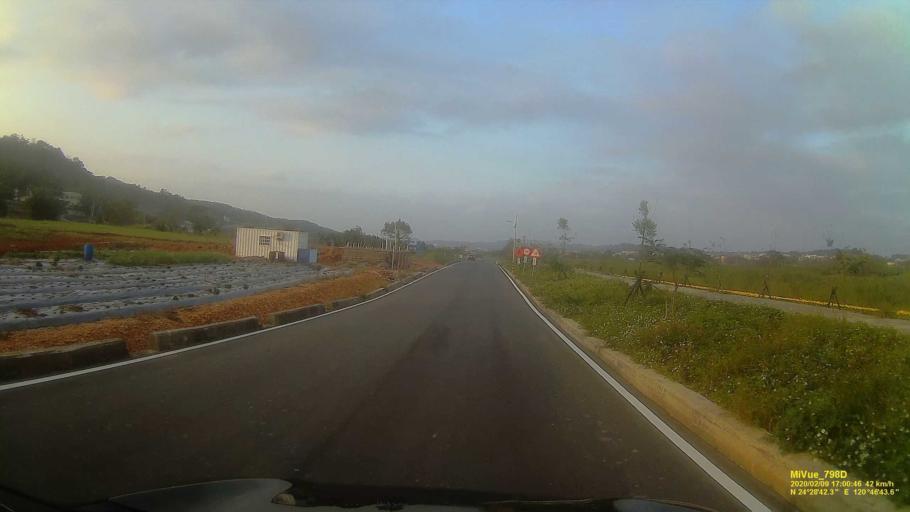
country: TW
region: Taiwan
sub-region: Miaoli
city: Miaoli
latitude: 24.4787
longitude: 120.7788
